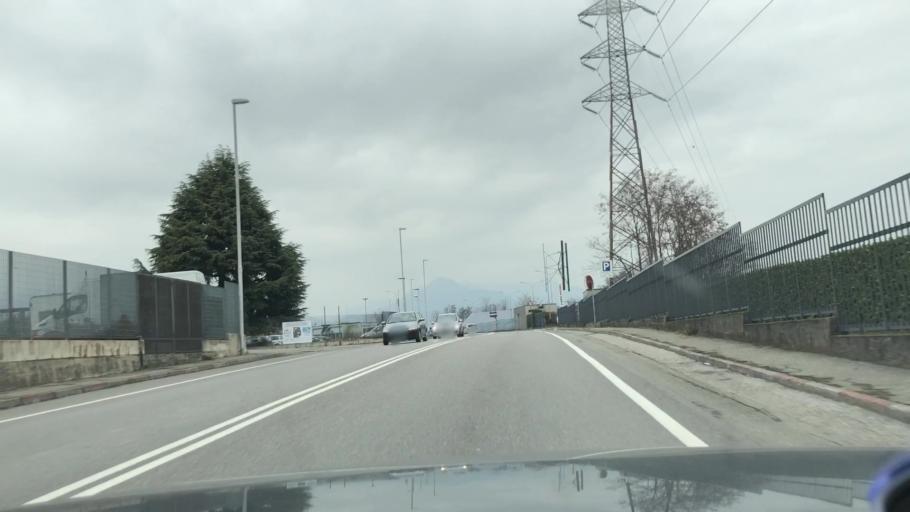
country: IT
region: Lombardy
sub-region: Provincia di Bergamo
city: Ponte San Pietro
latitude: 45.7057
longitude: 9.5836
